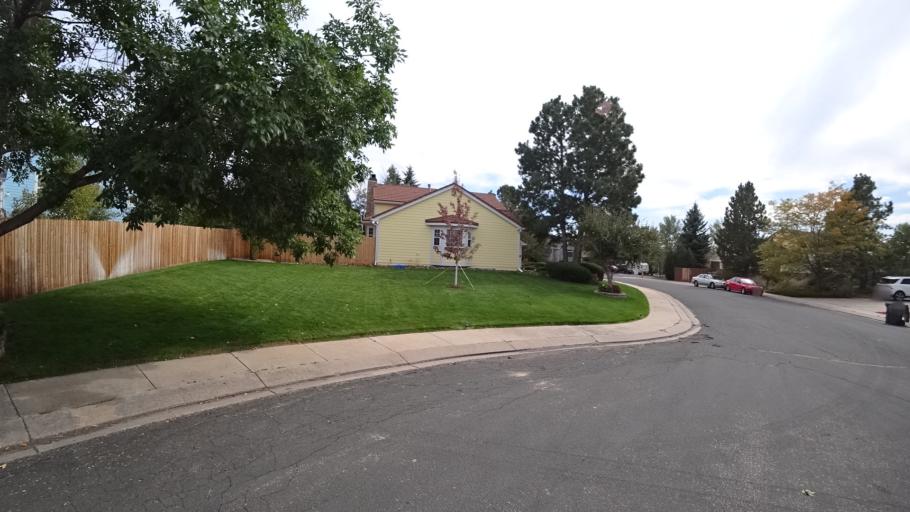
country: US
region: Colorado
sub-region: El Paso County
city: Cimarron Hills
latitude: 38.9007
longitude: -104.7040
